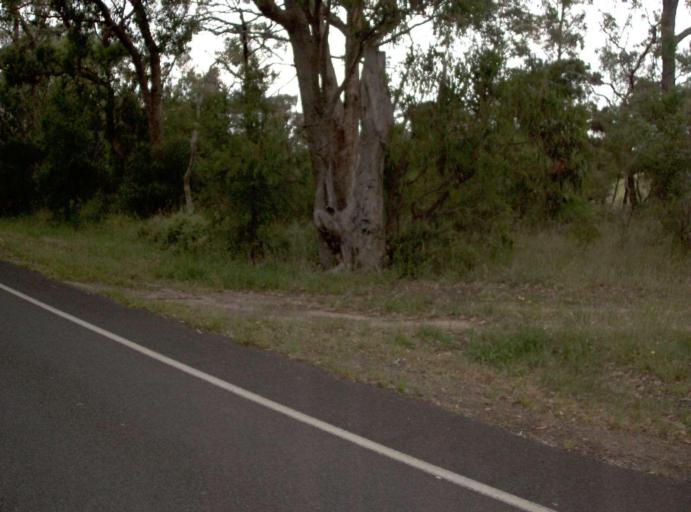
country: AU
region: Victoria
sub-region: Latrobe
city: Traralgon
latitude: -38.5446
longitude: 146.8332
